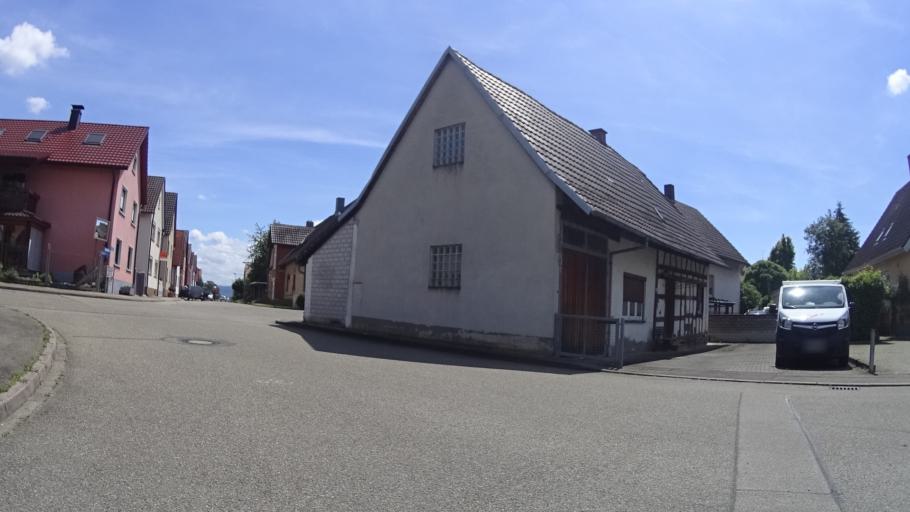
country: DE
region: Baden-Wuerttemberg
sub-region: Freiburg Region
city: Kappel-Grafenhausen
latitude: 48.2967
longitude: 7.7436
